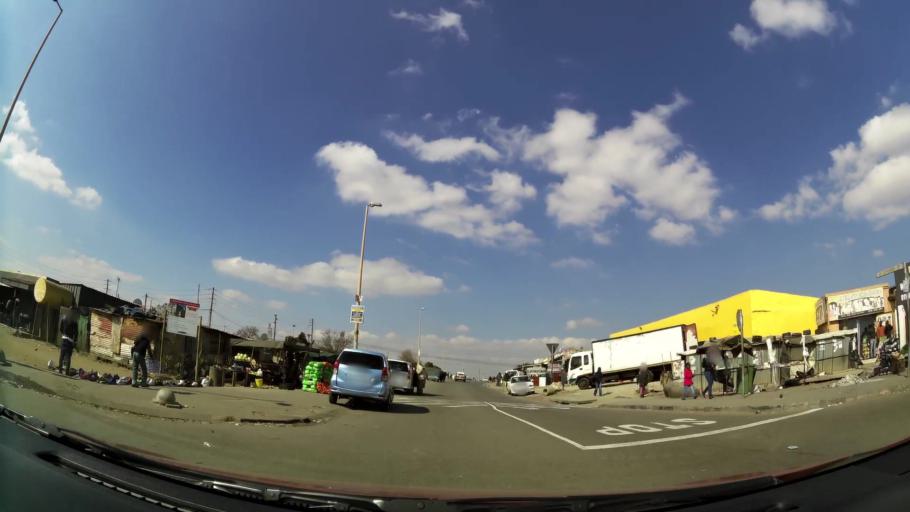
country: ZA
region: Gauteng
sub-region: Ekurhuleni Metropolitan Municipality
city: Tembisa
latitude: -26.0072
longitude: 28.1827
